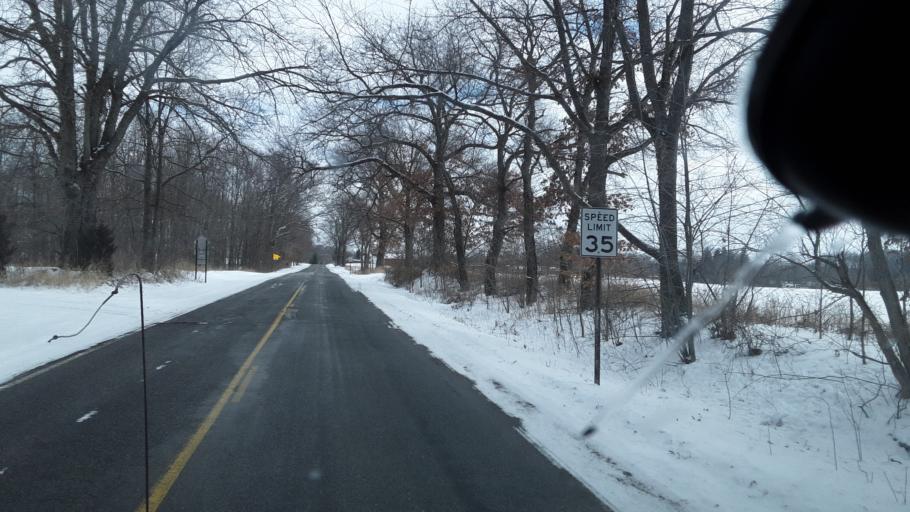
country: US
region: Michigan
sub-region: Ingham County
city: Leslie
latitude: 42.4753
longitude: -84.3248
